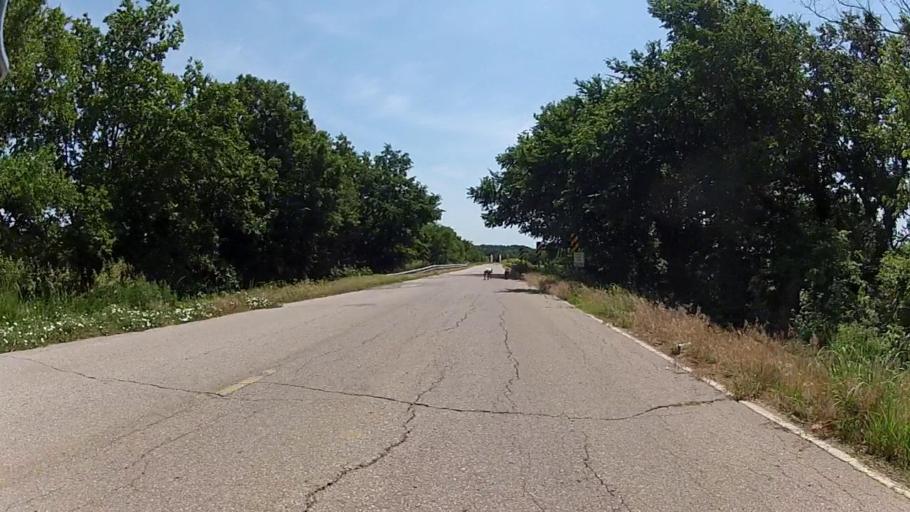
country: US
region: Kansas
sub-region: Chautauqua County
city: Sedan
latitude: 37.1064
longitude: -96.4887
